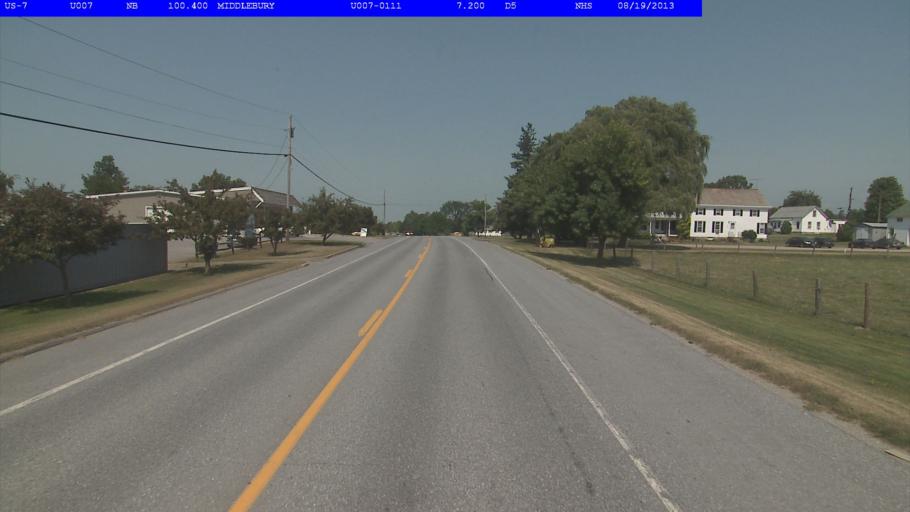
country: US
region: Vermont
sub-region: Addison County
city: Middlebury (village)
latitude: 44.0430
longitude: -73.1623
